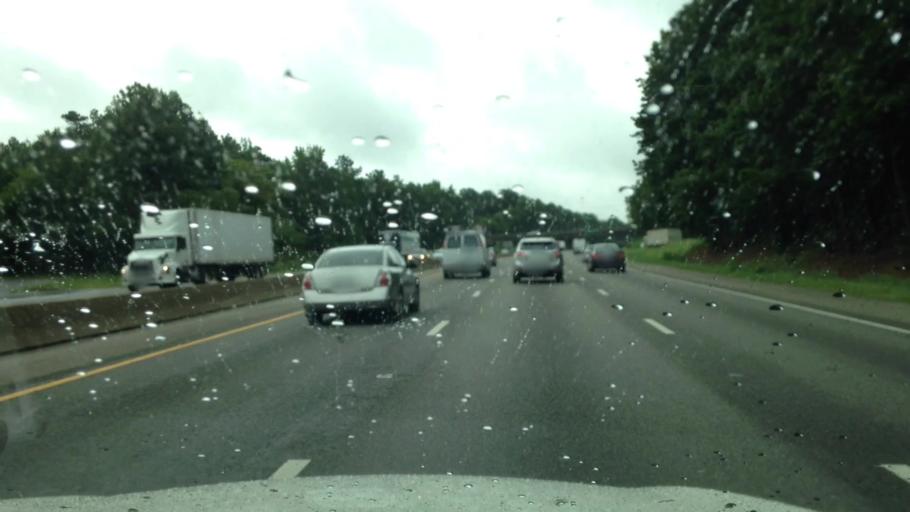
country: US
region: Virginia
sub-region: Chesterfield County
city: Chester
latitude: 37.3770
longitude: -77.4082
